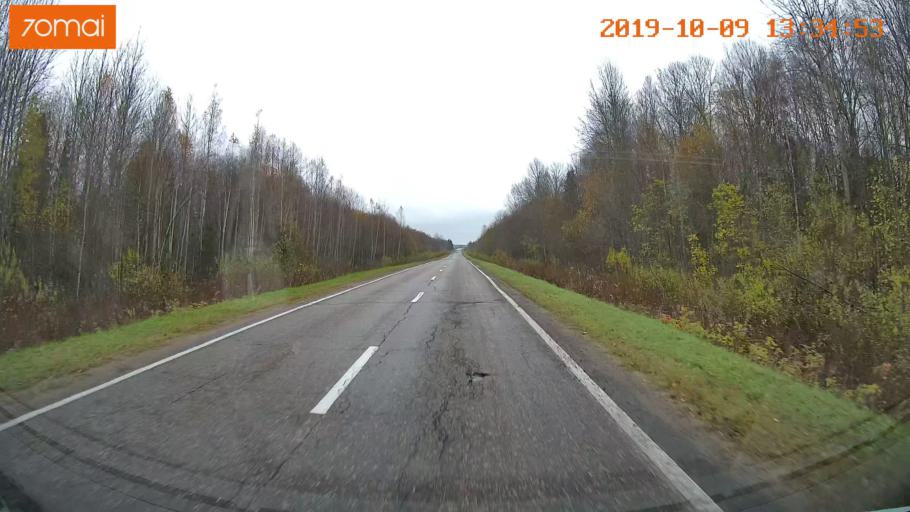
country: RU
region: Jaroslavl
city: Lyubim
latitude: 58.3326
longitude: 41.0679
